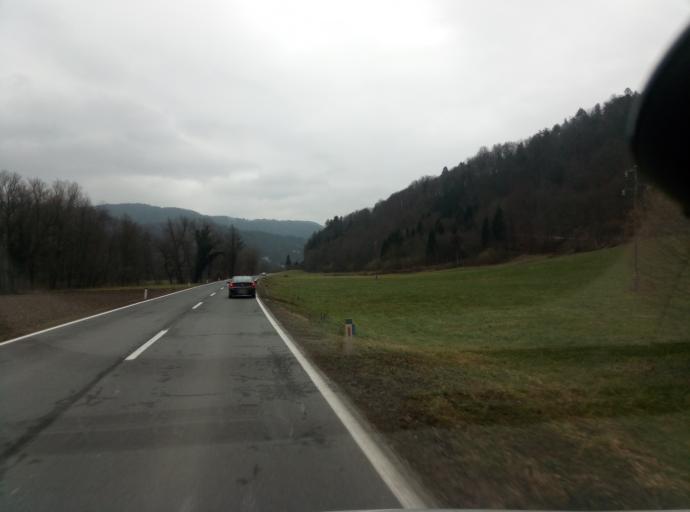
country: SI
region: Smartno pri Litiji
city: Smartno pri Litiji
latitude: 46.0776
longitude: 14.8720
